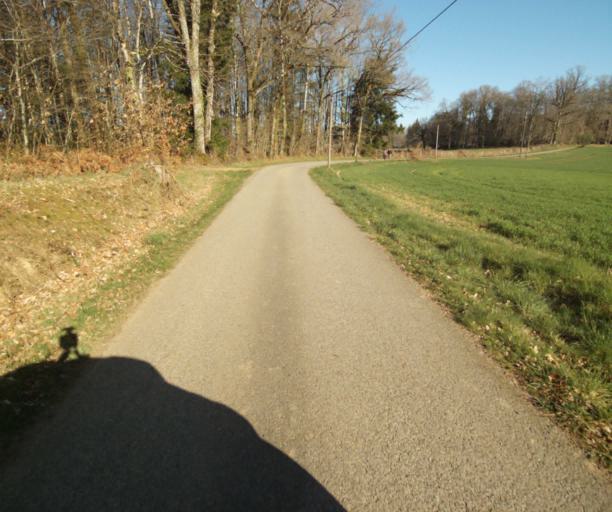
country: FR
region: Limousin
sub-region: Departement de la Correze
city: Uzerche
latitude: 45.3825
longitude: 1.6251
